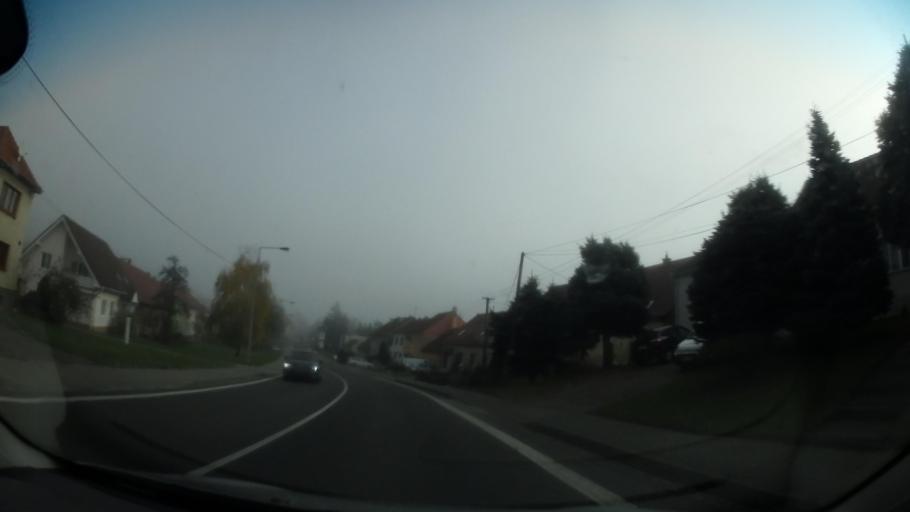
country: CZ
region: South Moravian
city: Zdanice
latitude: 49.0431
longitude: 17.0008
